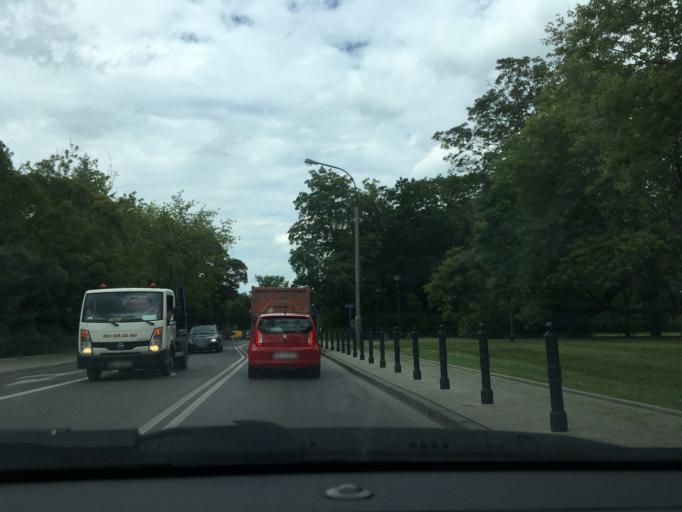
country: PL
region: Masovian Voivodeship
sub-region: Warszawa
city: Zoliborz
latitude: 52.2562
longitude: 21.0052
